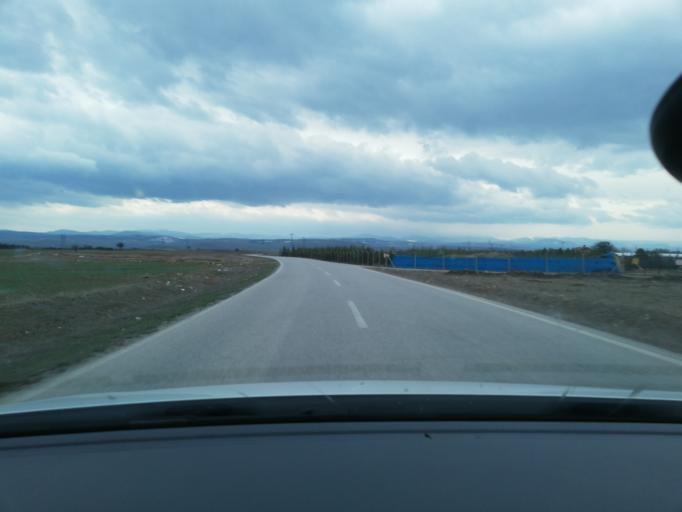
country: TR
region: Bolu
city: Gerede
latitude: 40.7696
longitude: 32.2024
